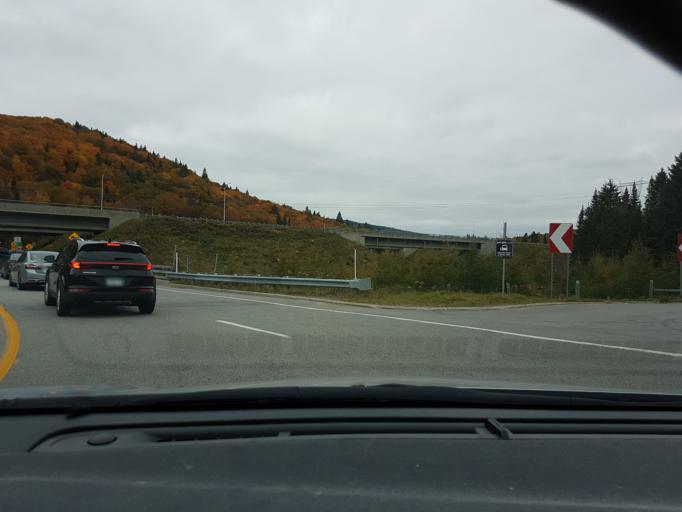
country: CA
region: Quebec
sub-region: Capitale-Nationale
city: Shannon
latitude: 47.1068
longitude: -71.3434
